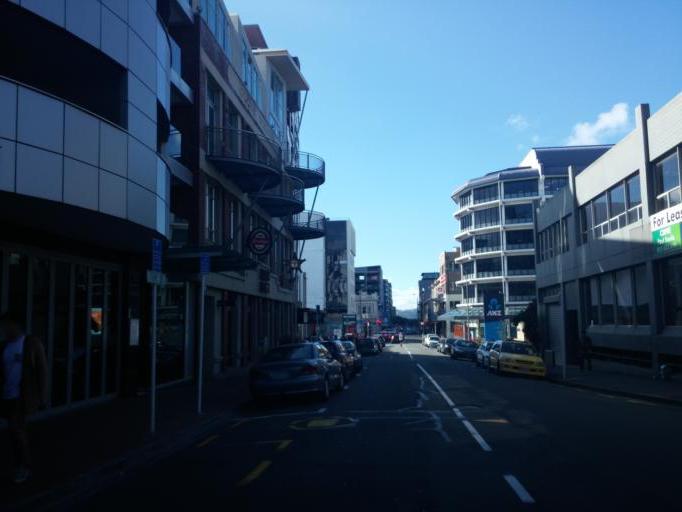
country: NZ
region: Wellington
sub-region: Wellington City
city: Wellington
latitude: -41.2948
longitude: 174.7805
